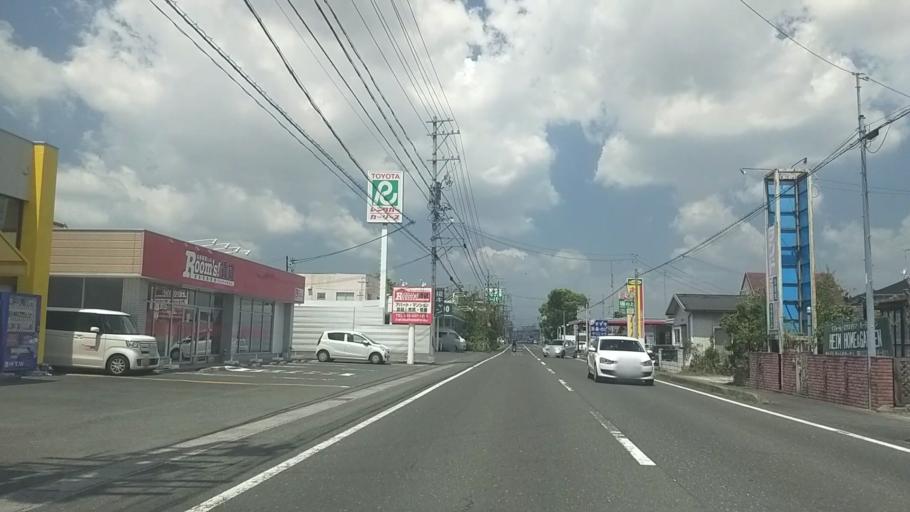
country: JP
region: Shizuoka
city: Hamamatsu
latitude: 34.7555
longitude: 137.7313
